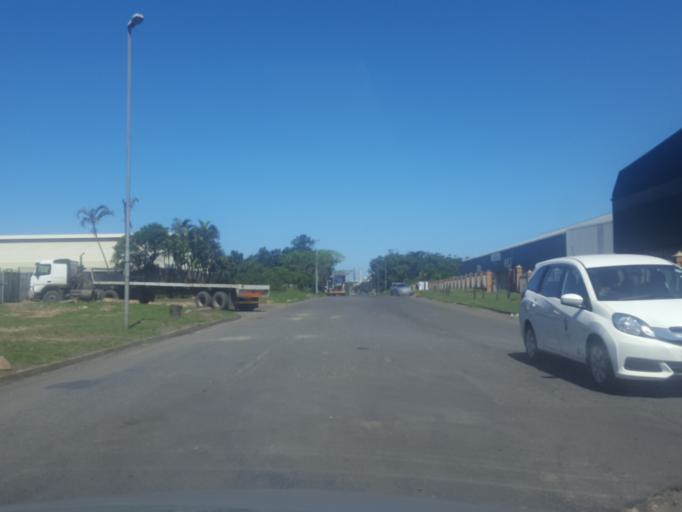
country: ZA
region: KwaZulu-Natal
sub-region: uThungulu District Municipality
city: Richards Bay
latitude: -28.7577
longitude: 32.0154
